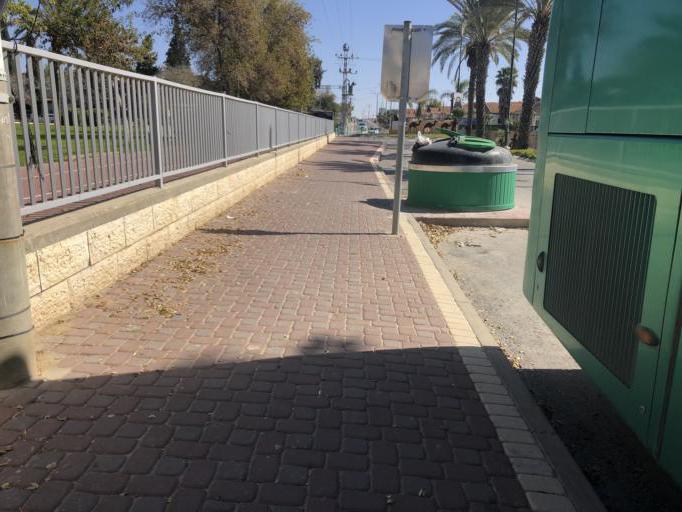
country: IL
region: Southern District
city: Dimona
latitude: 31.0668
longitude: 35.0391
